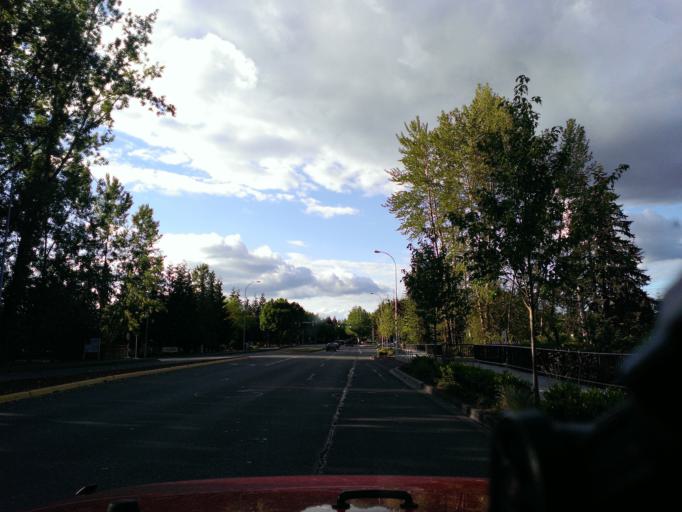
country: US
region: Washington
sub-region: King County
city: Redmond
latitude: 47.6565
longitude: -122.1432
